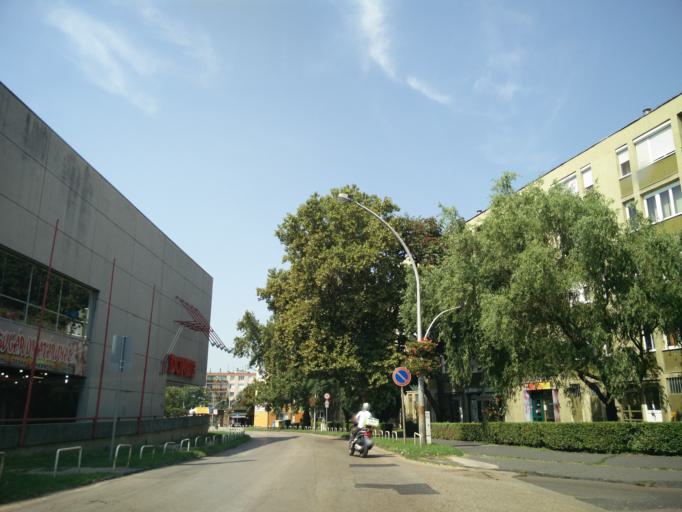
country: HU
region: Fejer
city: Szekesfehervar
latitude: 47.1956
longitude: 18.4080
